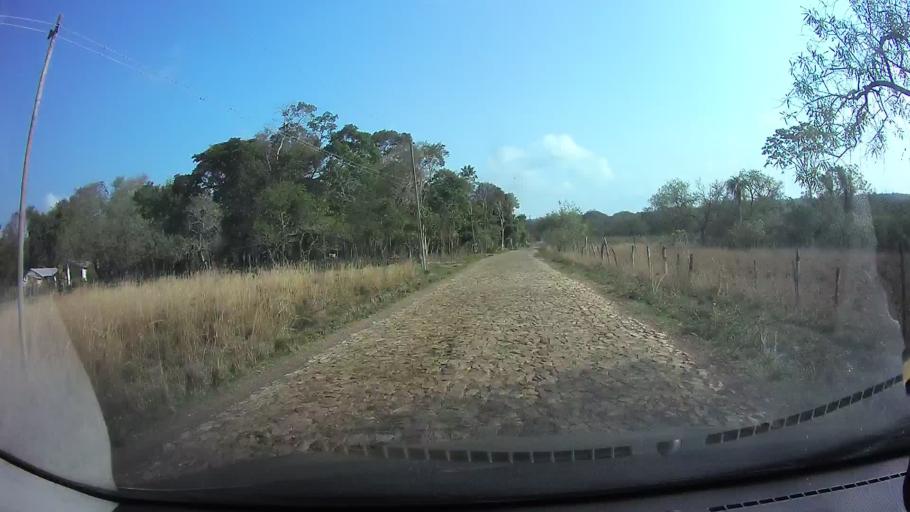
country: PY
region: Cordillera
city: Arroyos y Esteros
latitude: -25.0017
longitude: -57.1963
